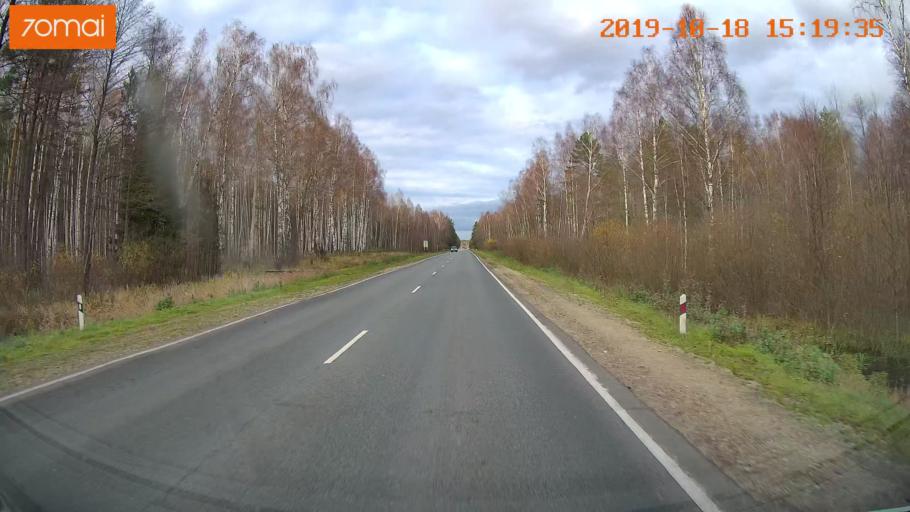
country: RU
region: Vladimir
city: Anopino
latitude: 55.6751
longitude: 40.7387
